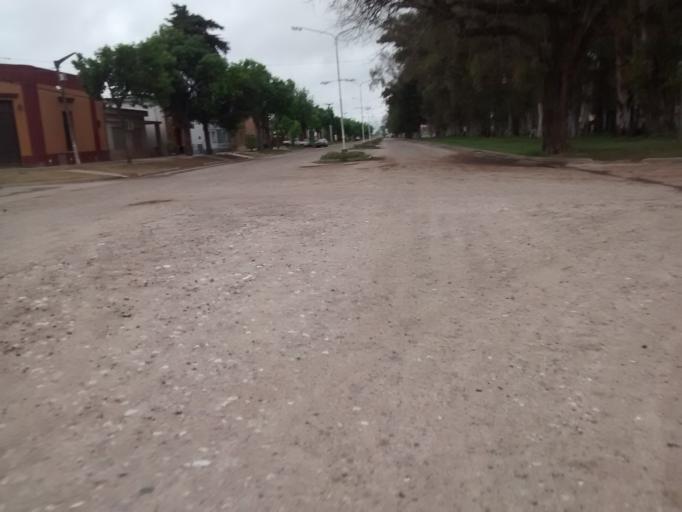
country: AR
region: Santa Fe
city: Galvez
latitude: -31.9024
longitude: -61.2814
